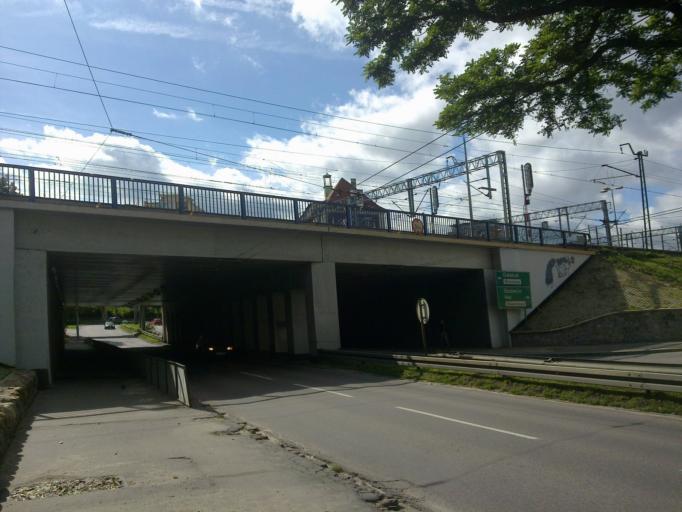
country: PL
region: Pomeranian Voivodeship
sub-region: Gdynia
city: Gdynia
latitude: 54.5194
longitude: 18.5331
